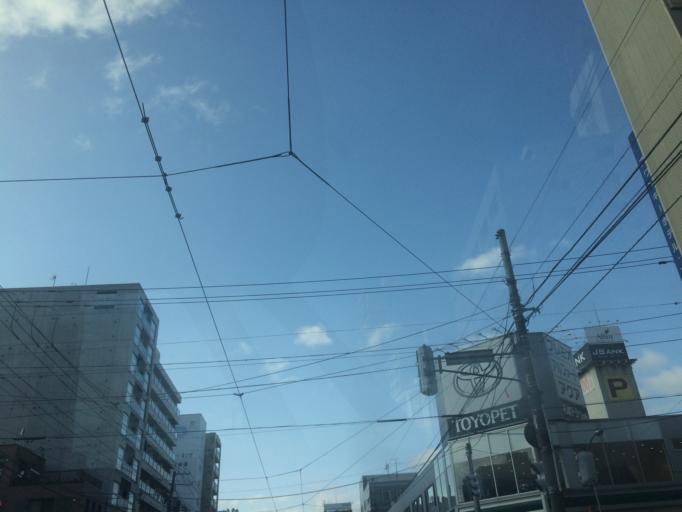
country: JP
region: Hokkaido
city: Sapporo
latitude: 43.0524
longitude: 141.3492
